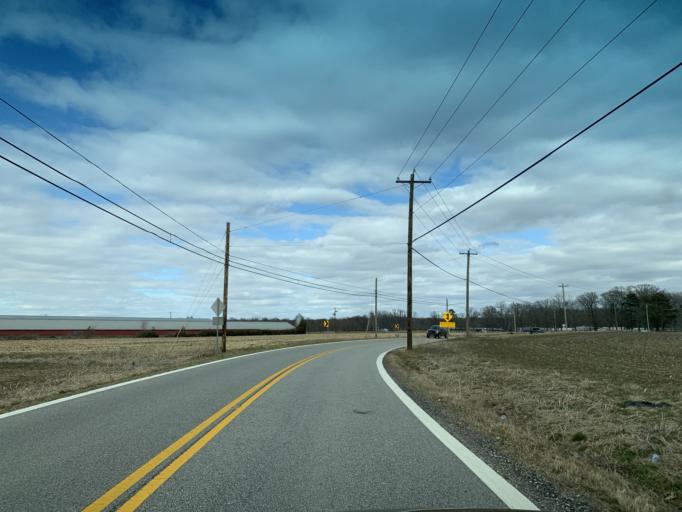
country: US
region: Maryland
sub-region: Queen Anne's County
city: Centreville
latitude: 39.0264
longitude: -76.1231
